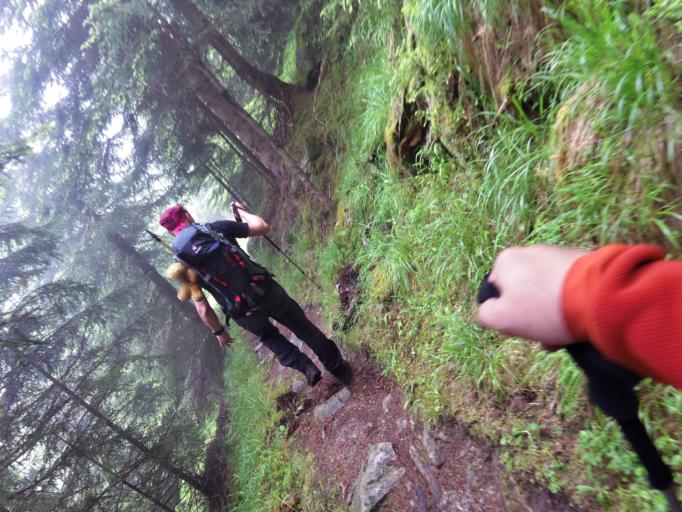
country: AT
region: Tyrol
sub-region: Politischer Bezirk Innsbruck Land
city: Neustift im Stubaital
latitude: 47.0511
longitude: 11.2252
